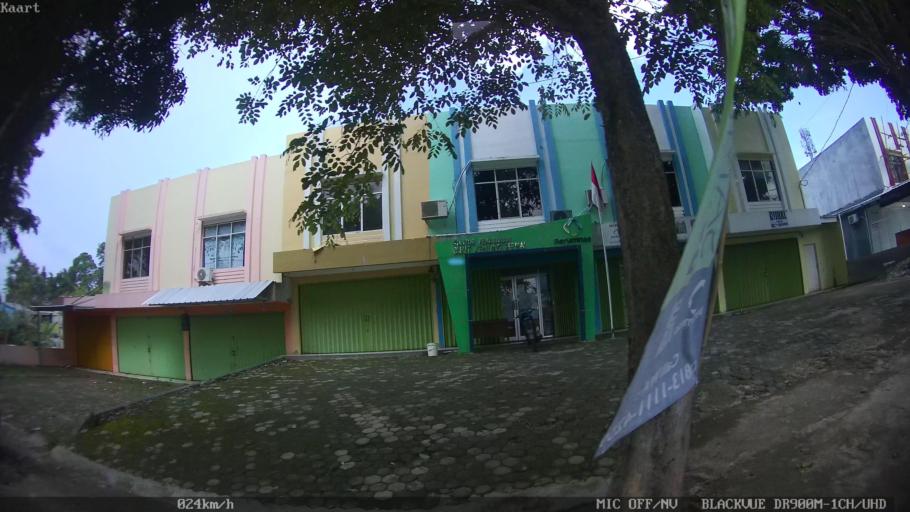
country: ID
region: Lampung
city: Kedaton
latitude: -5.3865
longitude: 105.2105
